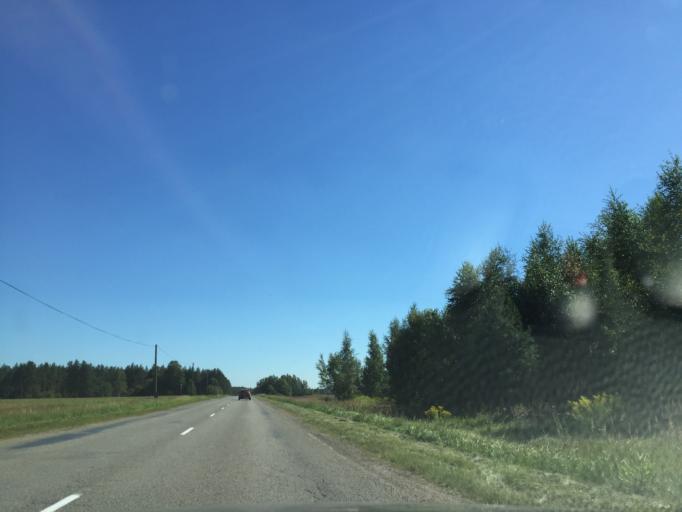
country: LV
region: Akniste
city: Akniste
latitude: 56.1337
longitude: 25.8240
